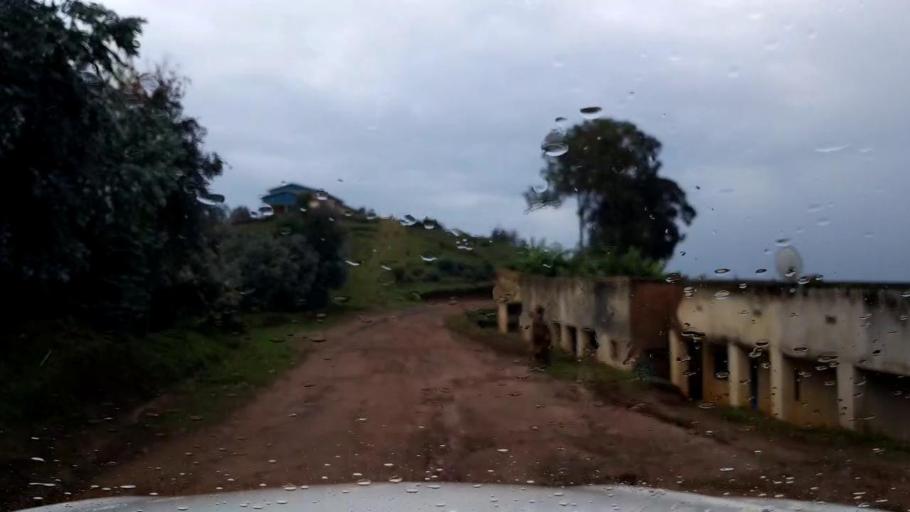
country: RW
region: Western Province
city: Kibuye
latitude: -2.0222
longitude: 29.4591
